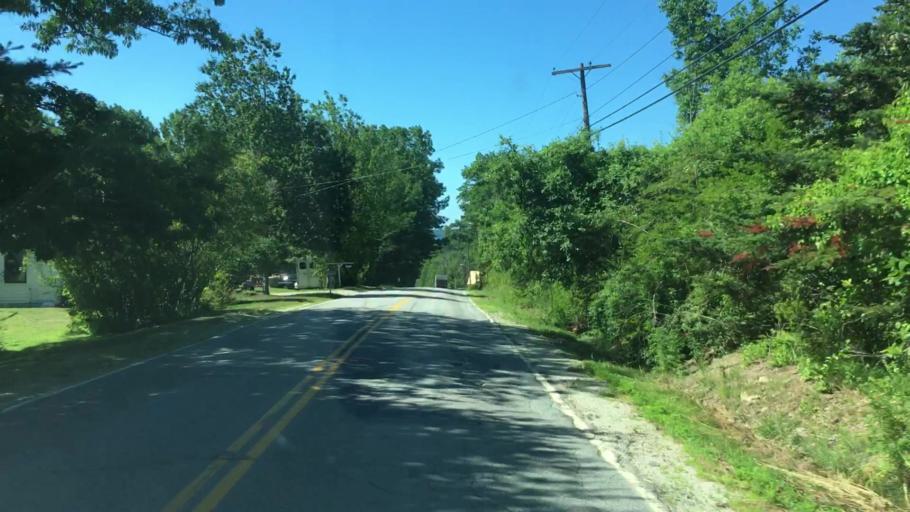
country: US
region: Maine
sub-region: Hancock County
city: Sedgwick
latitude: 44.3191
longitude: -68.6104
